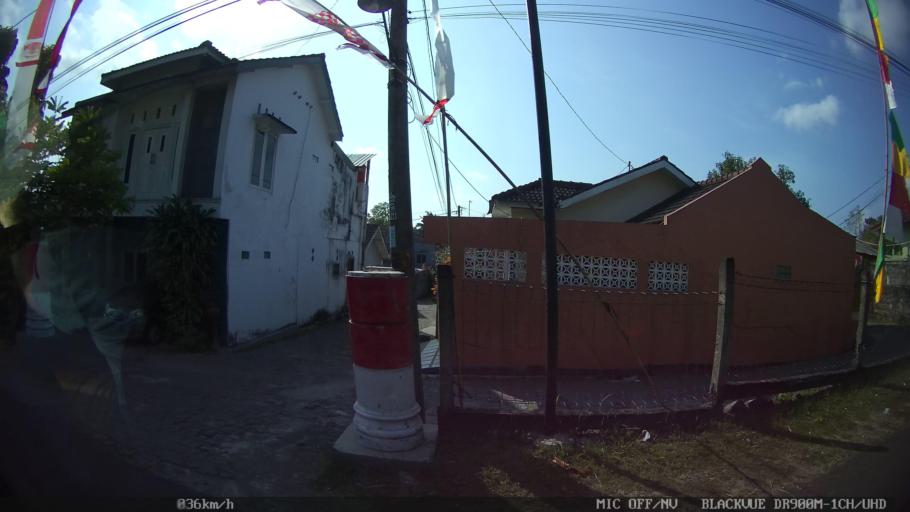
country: ID
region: Daerah Istimewa Yogyakarta
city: Kasihan
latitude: -7.8219
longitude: 110.2924
